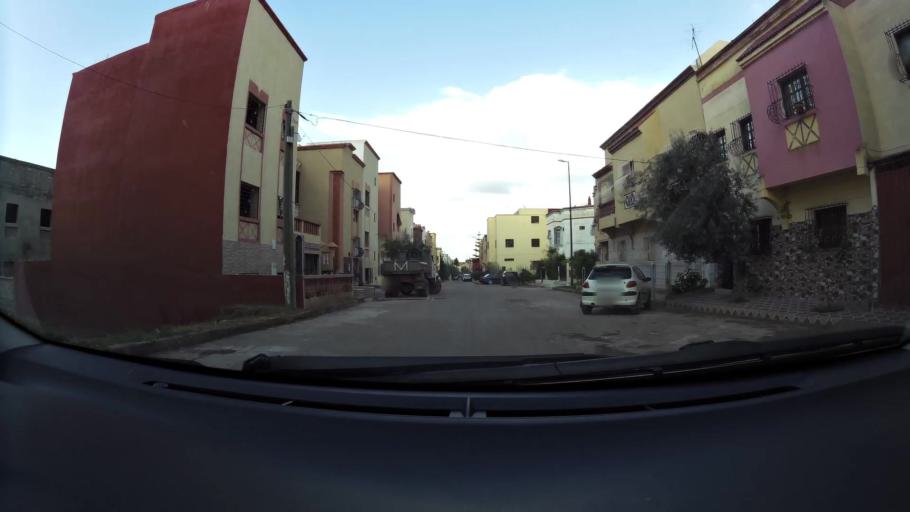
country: MA
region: Chaouia-Ouardigha
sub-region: Settat Province
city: Settat
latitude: 33.0057
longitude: -7.6383
